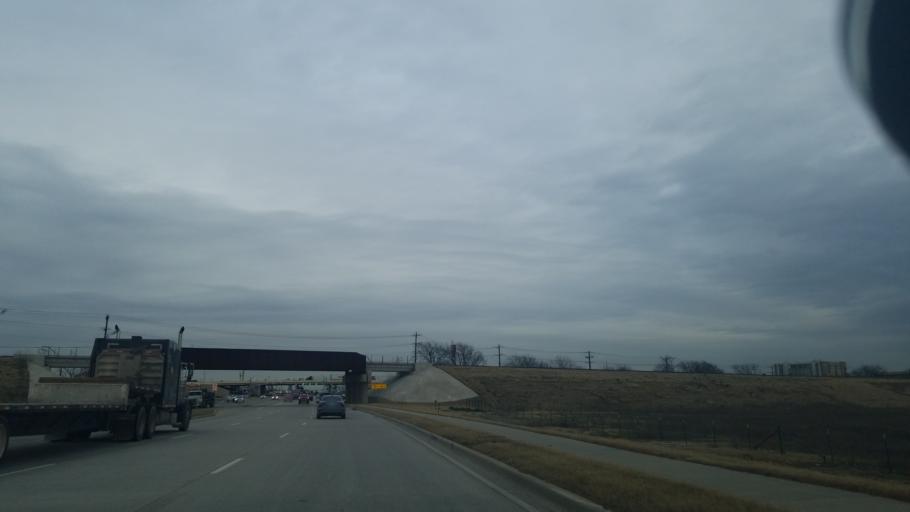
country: US
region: Texas
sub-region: Denton County
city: Denton
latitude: 33.2300
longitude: -97.1787
